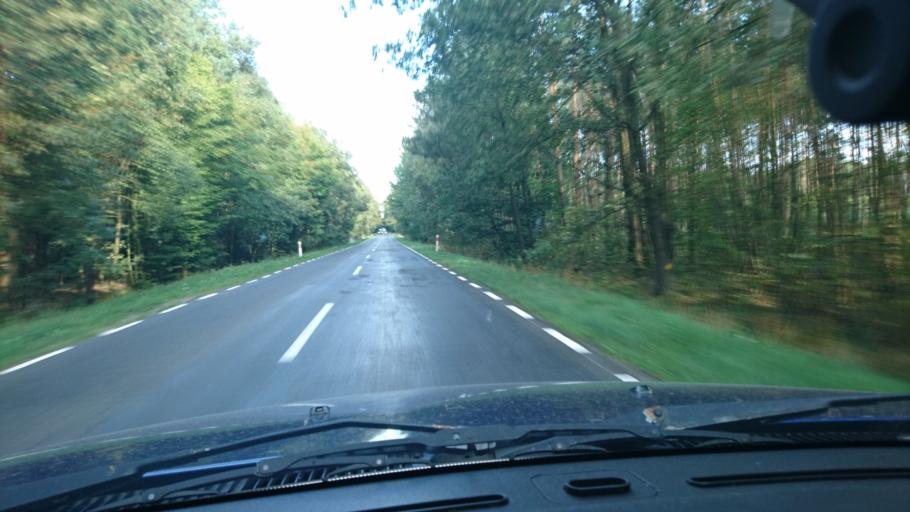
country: PL
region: Greater Poland Voivodeship
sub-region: Powiat krotoszynski
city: Sulmierzyce
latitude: 51.6000
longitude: 17.5964
